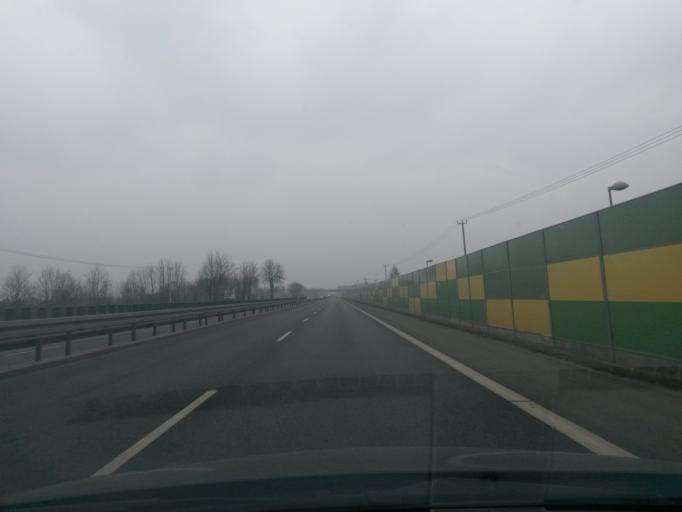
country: PL
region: Masovian Voivodeship
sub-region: Powiat legionowski
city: Bialobrzegi
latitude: 52.4788
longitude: 21.0363
